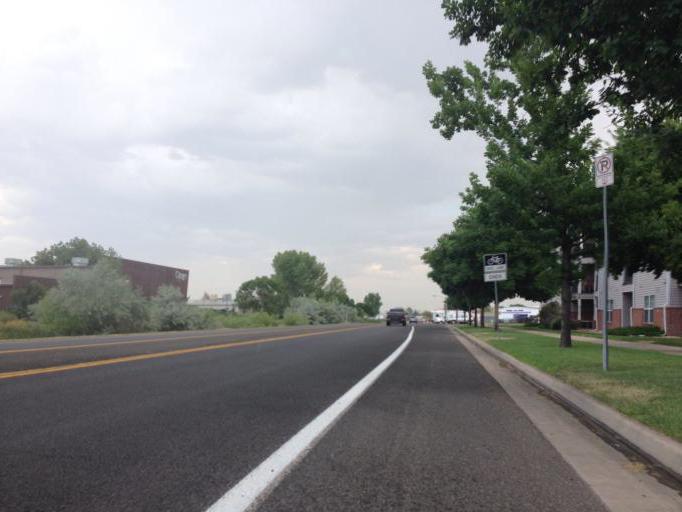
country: US
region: Colorado
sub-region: Larimer County
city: Fort Collins
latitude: 40.5882
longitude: -105.0541
